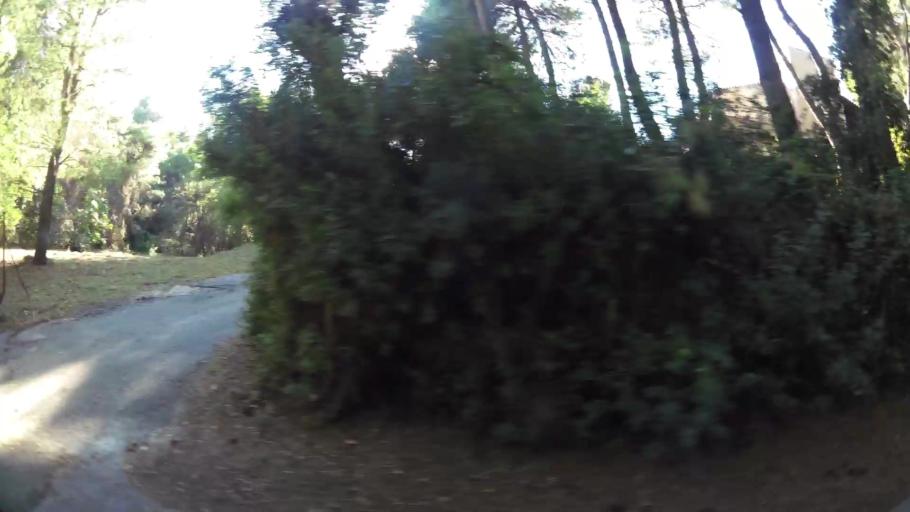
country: GR
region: Attica
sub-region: Nomarchia Athinas
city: Ekali
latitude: 38.1201
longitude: 23.8446
